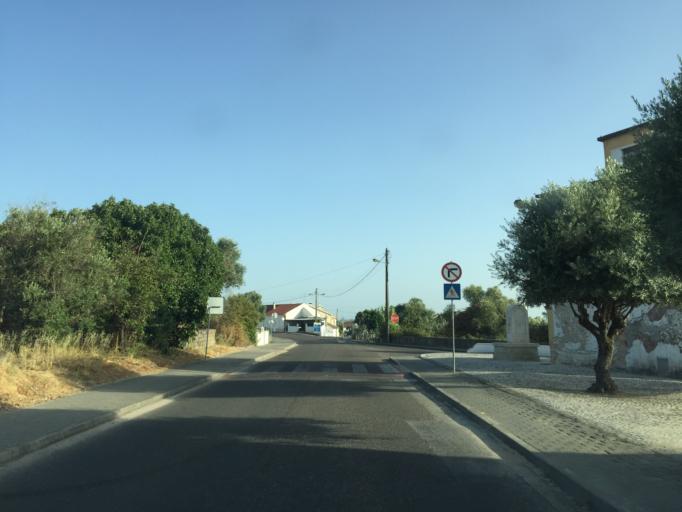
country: PT
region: Santarem
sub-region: Entroncamento
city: Entroncamento
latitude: 39.4782
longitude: -8.4521
